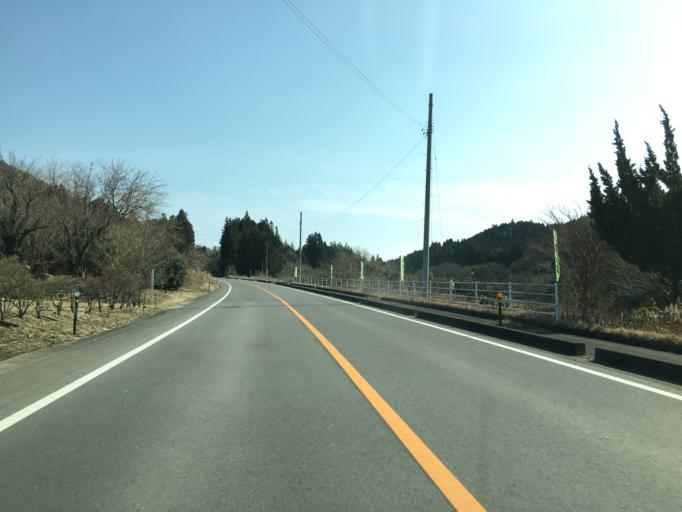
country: JP
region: Ibaraki
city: Daigo
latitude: 36.8129
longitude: 140.4647
